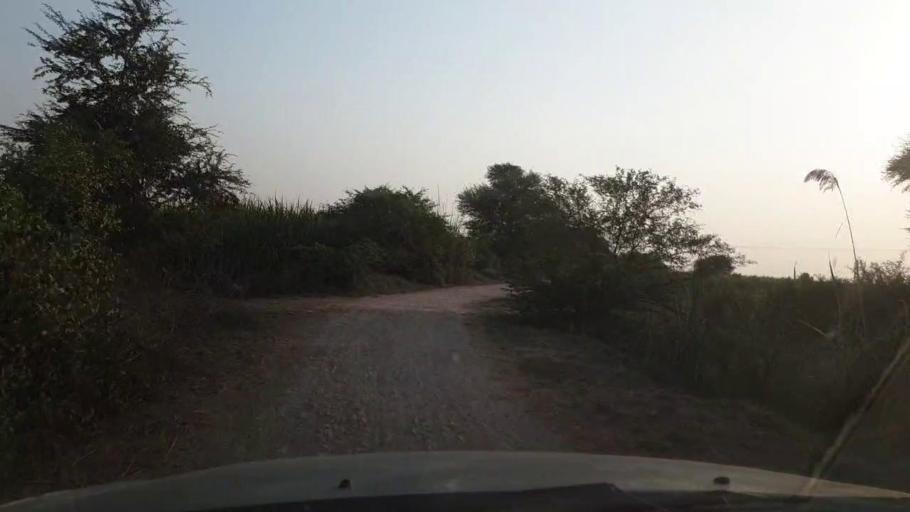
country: PK
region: Sindh
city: Tando Muhammad Khan
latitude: 25.0038
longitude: 68.4352
